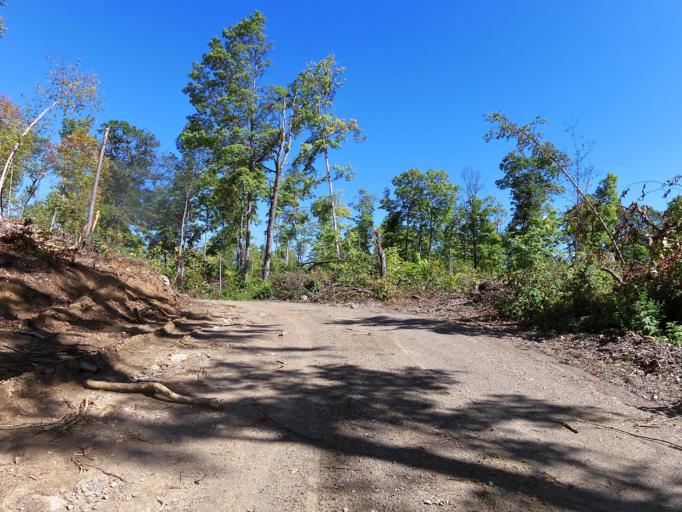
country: CA
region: Ontario
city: Renfrew
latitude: 45.1278
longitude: -76.7228
